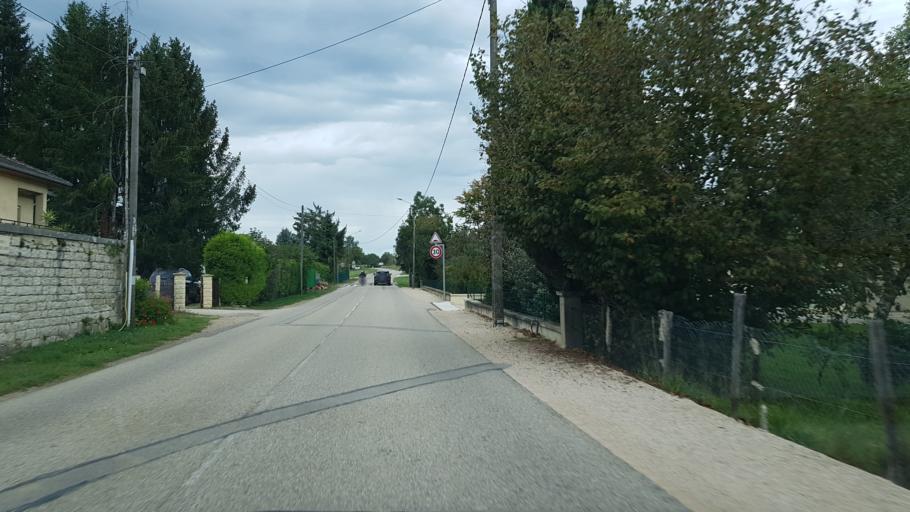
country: FR
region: Rhone-Alpes
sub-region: Departement de l'Ain
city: Cuisiat
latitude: 46.2674
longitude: 5.4265
